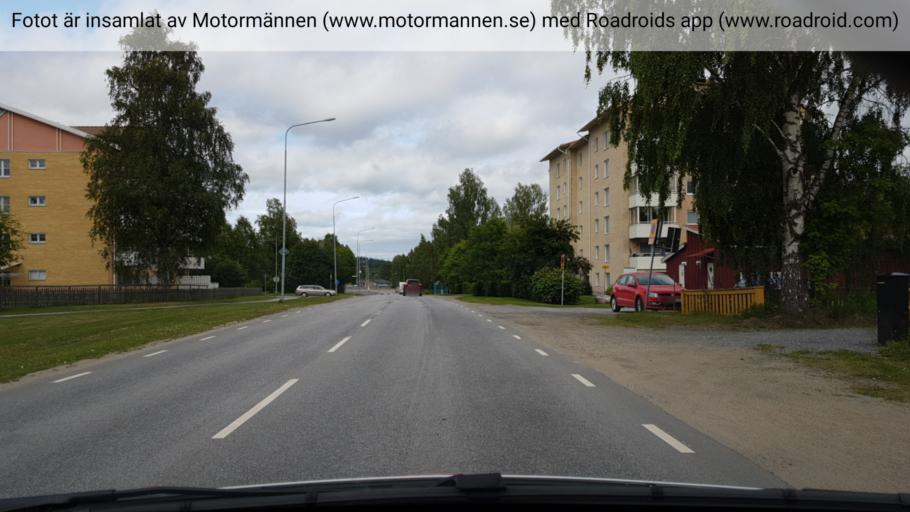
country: SE
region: Vaesterbotten
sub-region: Vannas Kommun
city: Vaennaes
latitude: 63.9068
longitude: 19.7655
